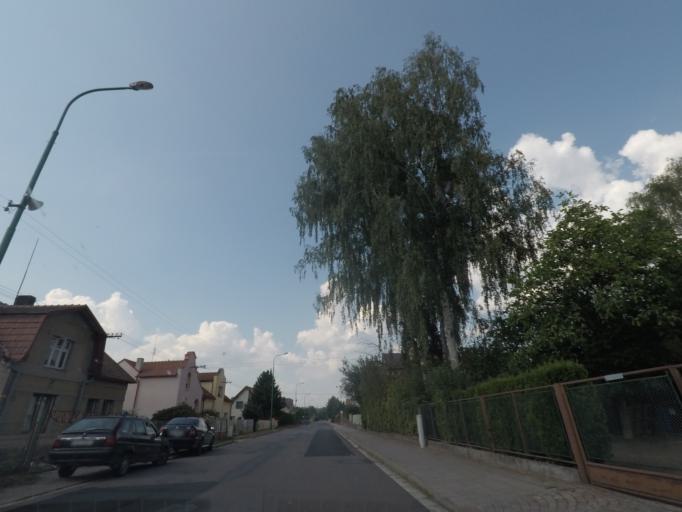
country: CZ
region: Pardubicky
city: Horni Jeleni
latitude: 50.0524
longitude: 16.0836
